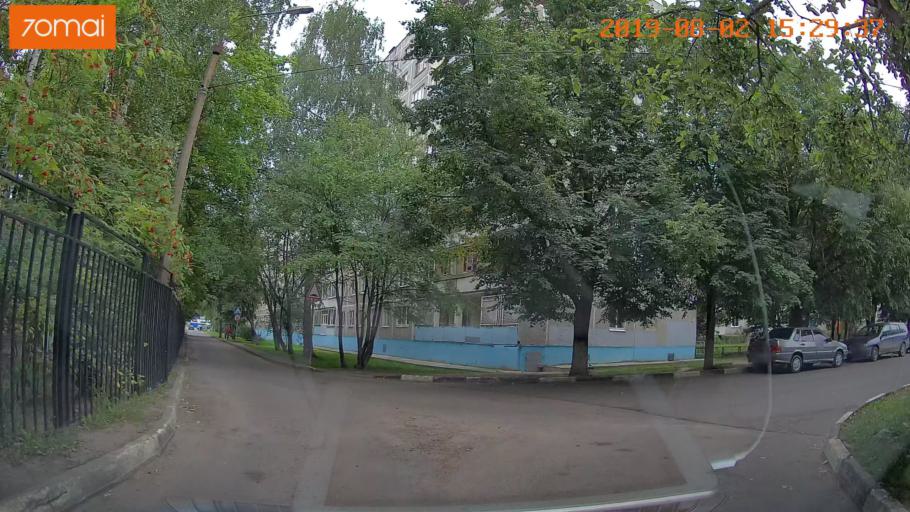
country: RU
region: Moskovskaya
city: Voskresensk
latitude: 55.3159
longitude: 38.6537
